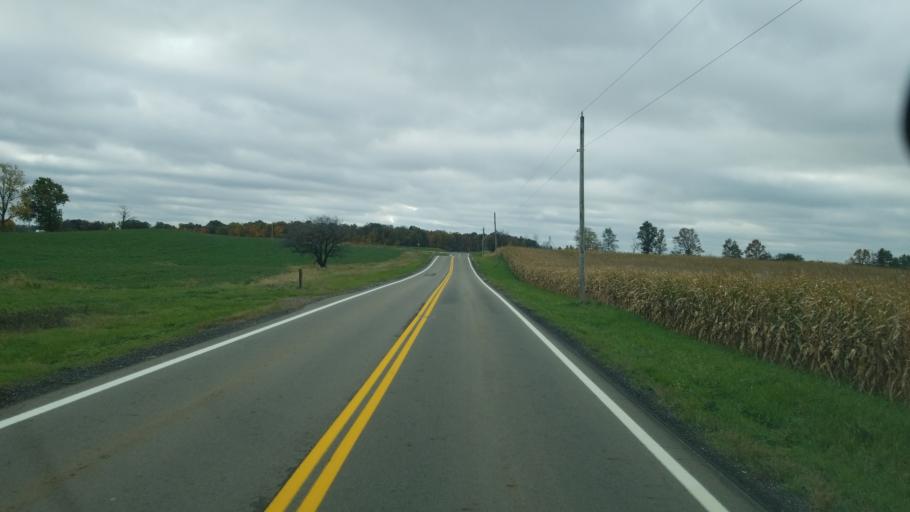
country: US
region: Ohio
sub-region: Richland County
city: Shelby
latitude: 40.9112
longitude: -82.7363
